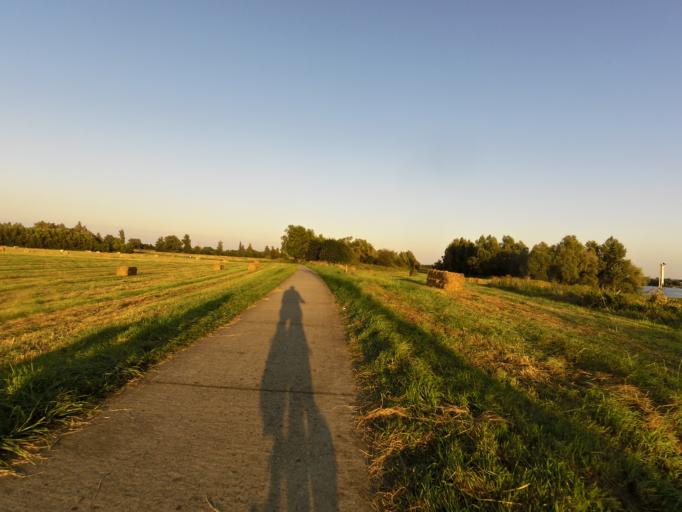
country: NL
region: Gelderland
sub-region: Gemeente Zevenaar
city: Zevenaar
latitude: 51.8681
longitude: 6.0643
